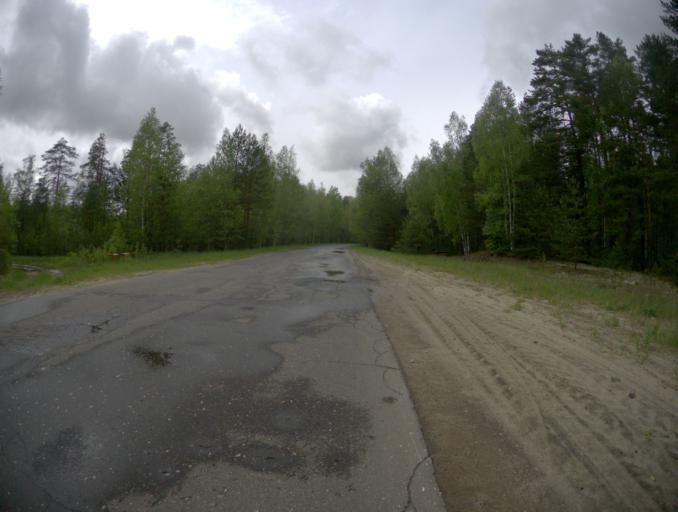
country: RU
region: Vladimir
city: Zolotkovo
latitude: 55.3480
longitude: 40.9461
